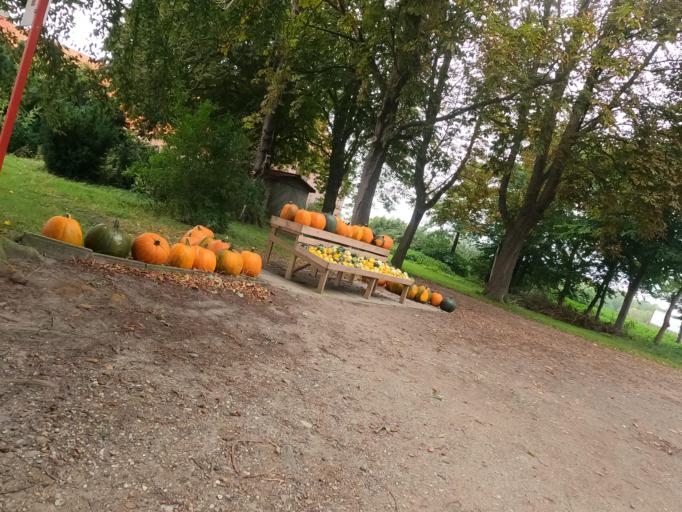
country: DE
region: Schleswig-Holstein
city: Heiligenhafen
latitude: 54.3557
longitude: 11.0108
